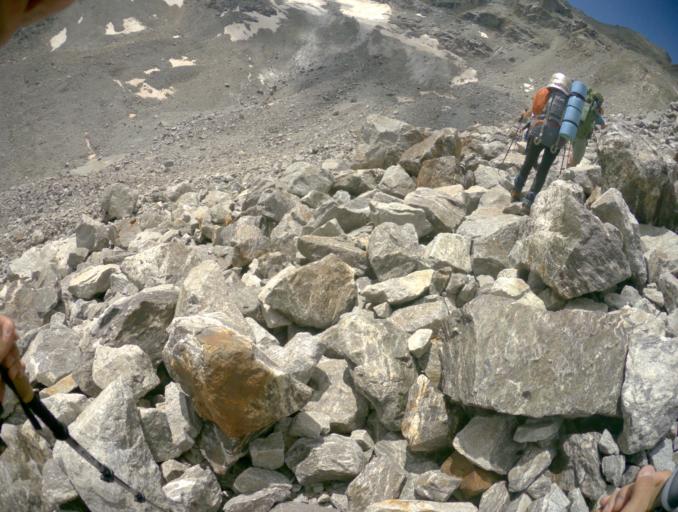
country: RU
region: Karachayevo-Cherkesiya
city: Uchkulan
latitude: 43.3224
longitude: 42.0872
